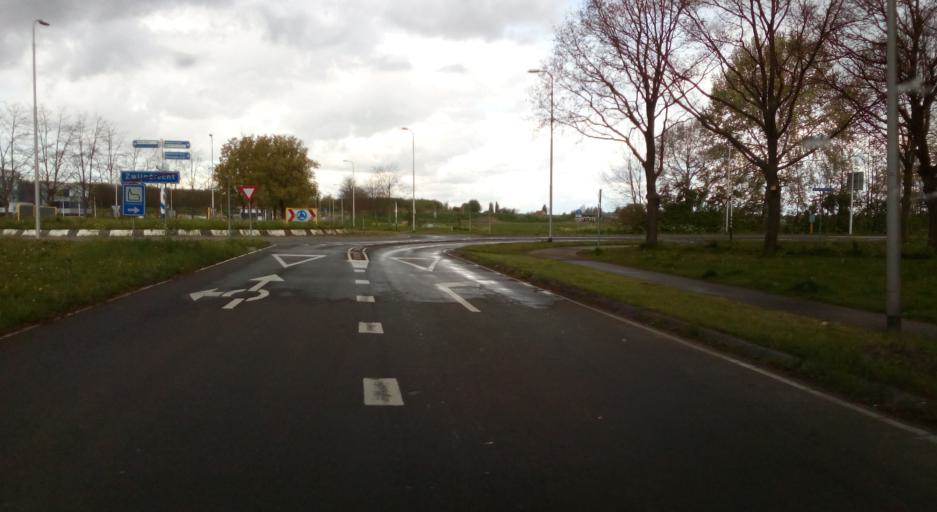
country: NL
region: South Holland
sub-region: Gemeente Zwijndrecht
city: Heerjansdam
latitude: 51.8134
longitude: 4.5940
